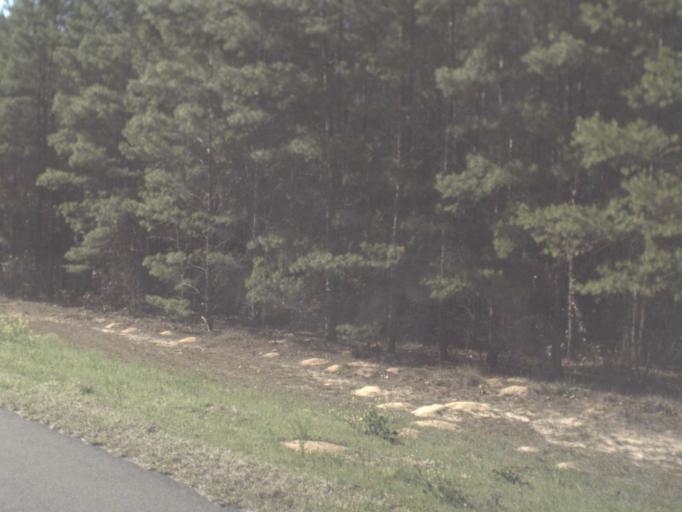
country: US
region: Florida
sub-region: Bay County
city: Youngstown
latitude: 30.4335
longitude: -85.2796
